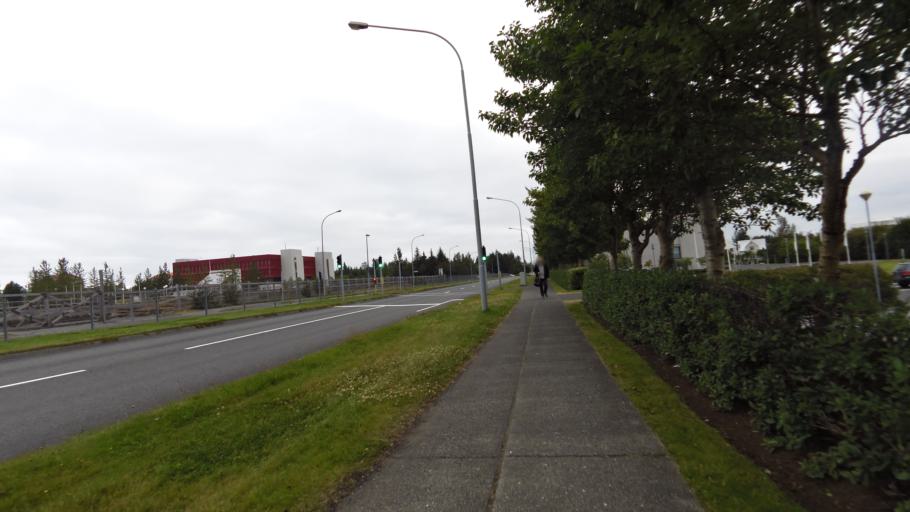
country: IS
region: Capital Region
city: Seltjarnarnes
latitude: 64.1409
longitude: -21.9502
